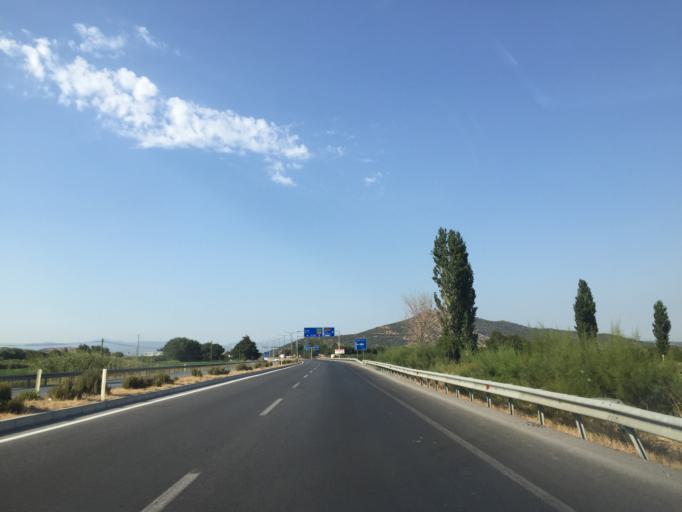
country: TR
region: Izmir
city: Belevi
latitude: 38.0176
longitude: 27.4390
